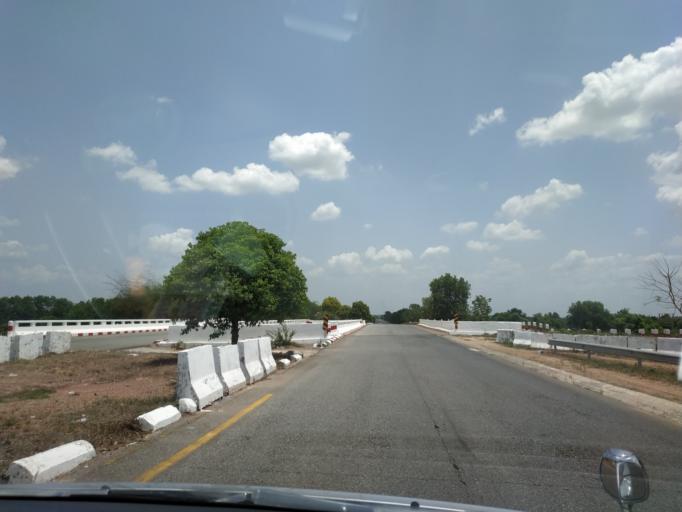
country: MM
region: Bago
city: Thanatpin
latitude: 17.1386
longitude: 96.1961
